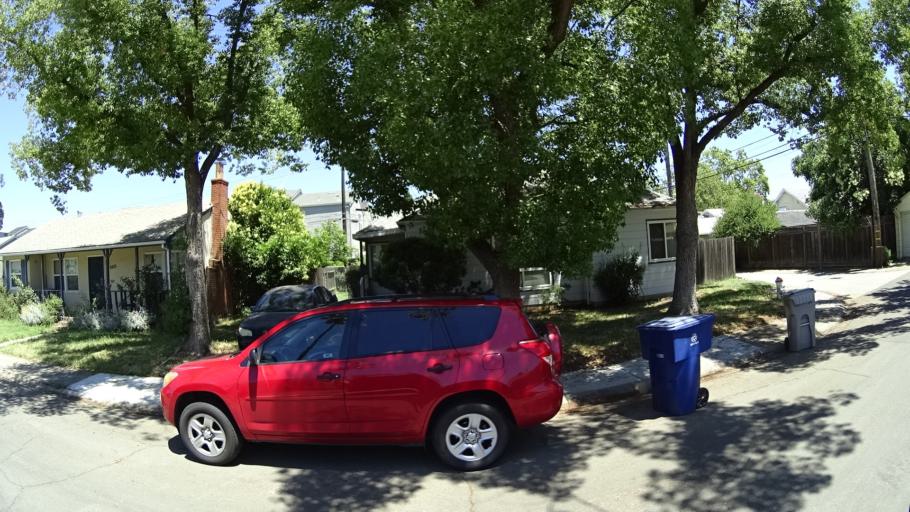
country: US
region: California
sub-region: Sacramento County
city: Sacramento
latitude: 38.5587
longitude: -121.4658
